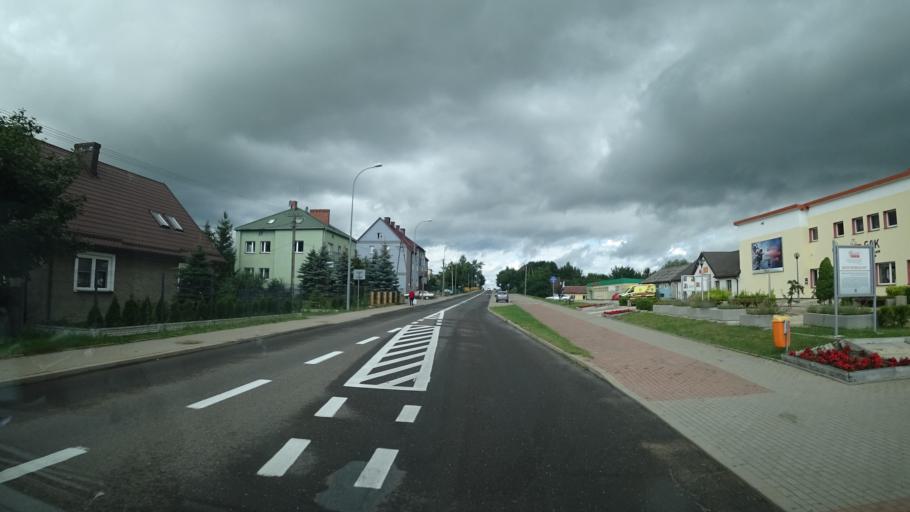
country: PL
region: Warmian-Masurian Voivodeship
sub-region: Powiat olecki
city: Kowale Oleckie
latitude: 54.1633
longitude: 22.4162
